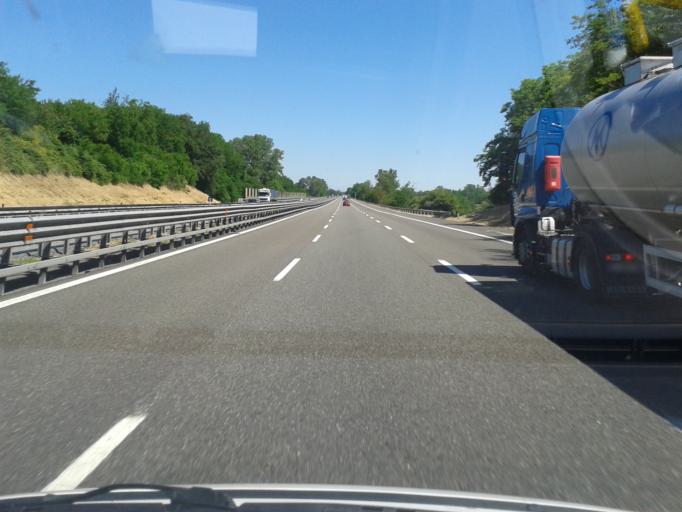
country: IT
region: Piedmont
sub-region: Provincia di Alessandria
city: Silvano d'Orba
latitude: 44.6912
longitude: 8.6653
